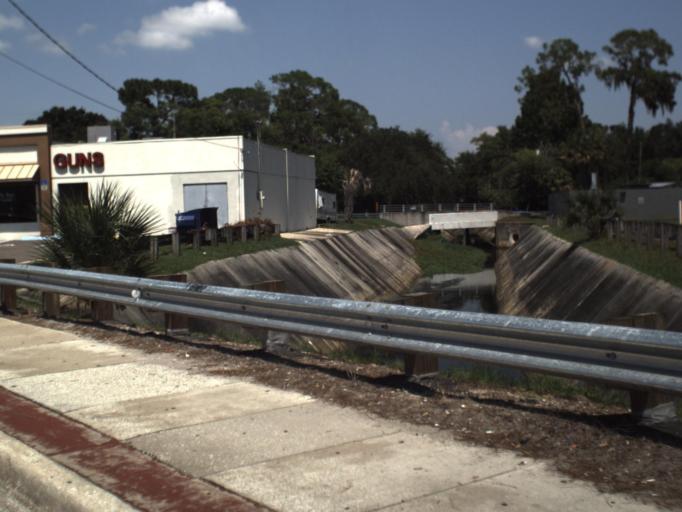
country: US
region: Florida
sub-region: Pinellas County
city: Kenneth City
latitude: 27.8276
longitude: -82.7284
